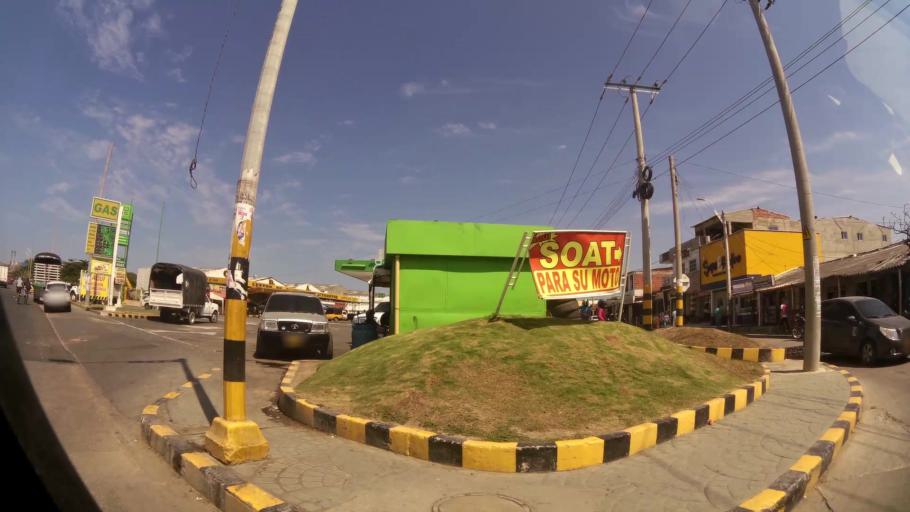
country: CO
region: Atlantico
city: Barranquilla
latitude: 10.9747
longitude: -74.8363
